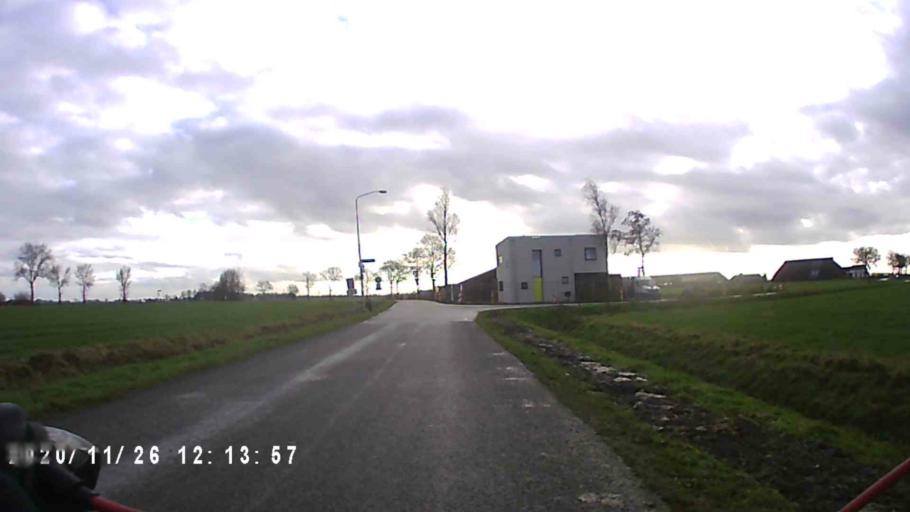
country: NL
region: Groningen
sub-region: Gemeente Bedum
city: Bedum
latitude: 53.3394
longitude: 6.6498
